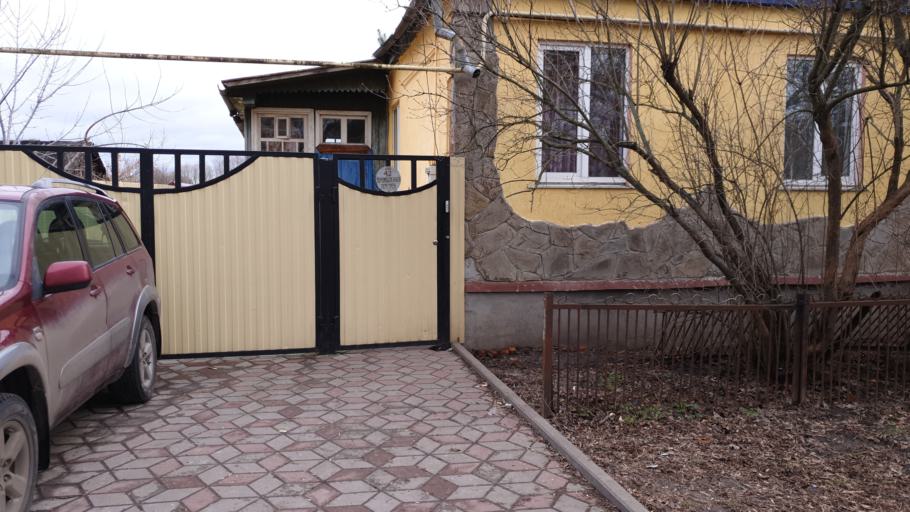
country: RU
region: Kursk
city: Voroshnevo
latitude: 51.6705
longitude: 36.0953
